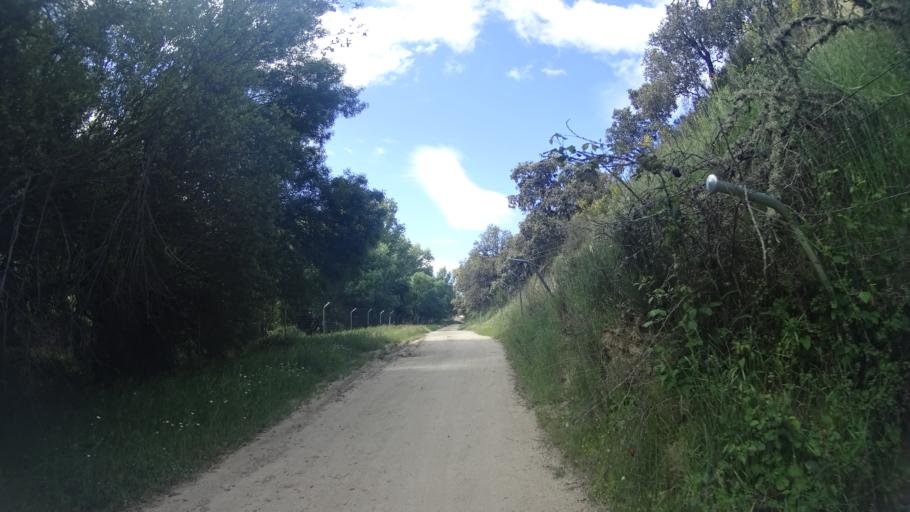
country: ES
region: Madrid
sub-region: Provincia de Madrid
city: Villanueva del Pardillo
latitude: 40.4324
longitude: -3.9530
